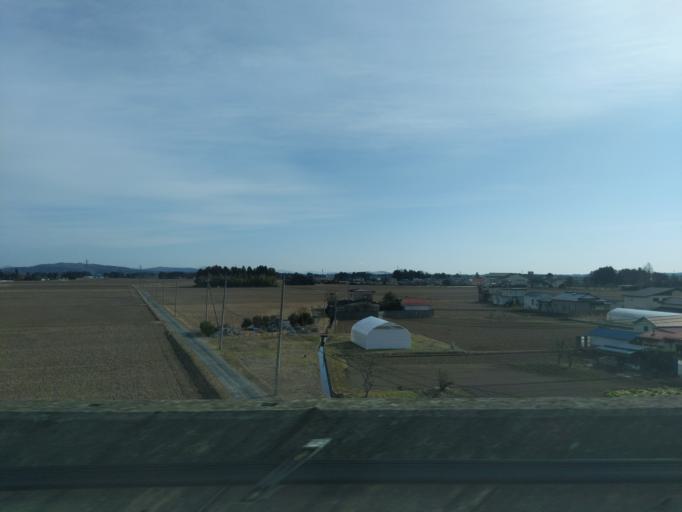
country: JP
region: Miyagi
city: Furukawa
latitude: 38.5987
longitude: 140.9816
